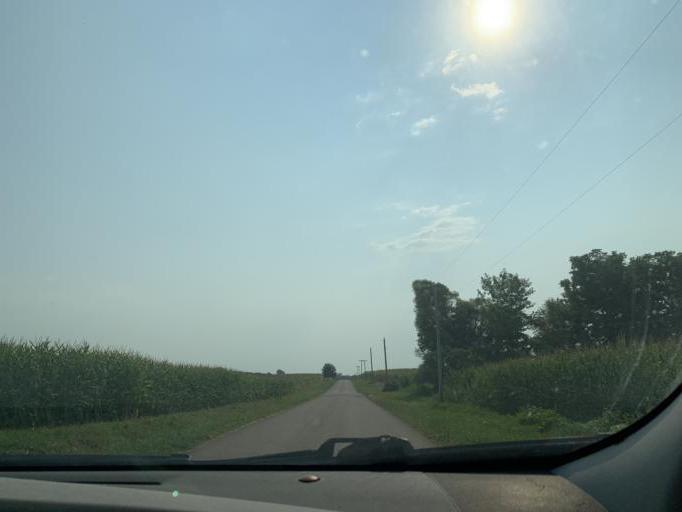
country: US
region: Illinois
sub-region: Whiteside County
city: Morrison
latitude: 41.8698
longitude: -89.8913
